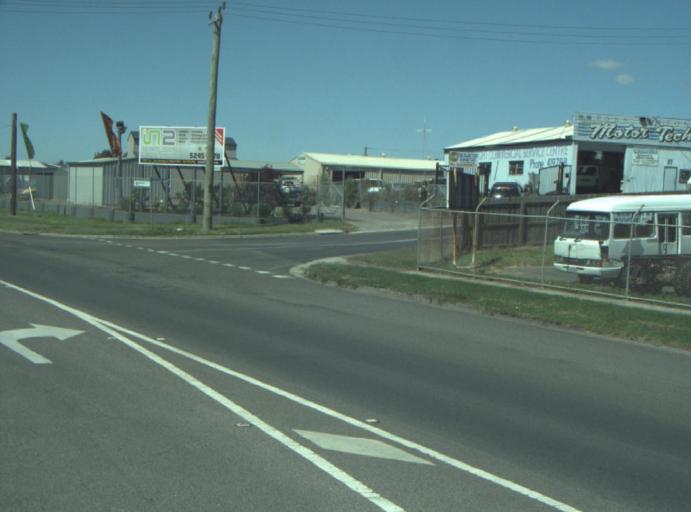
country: AU
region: Victoria
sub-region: Greater Geelong
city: Breakwater
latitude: -38.1834
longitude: 144.3543
